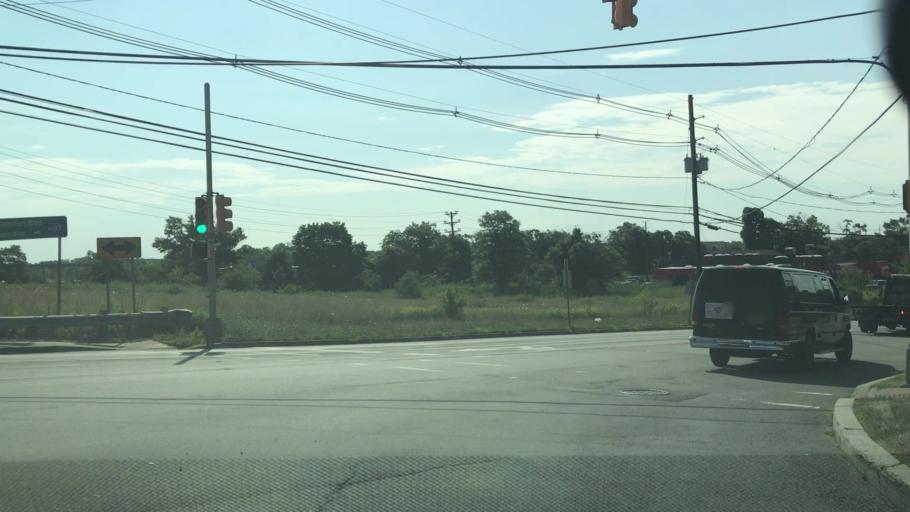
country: US
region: New Jersey
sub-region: Middlesex County
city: South Plainfield
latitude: 40.5594
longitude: -74.4178
